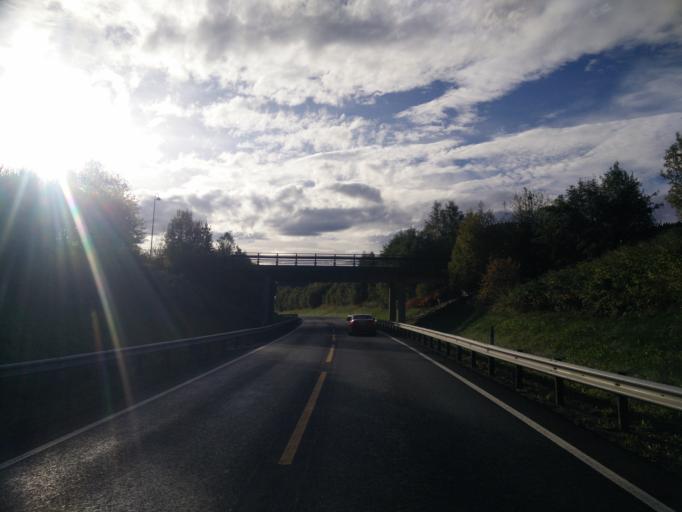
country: NO
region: More og Romsdal
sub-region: Vestnes
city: Vestnes
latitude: 62.6166
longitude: 7.0878
